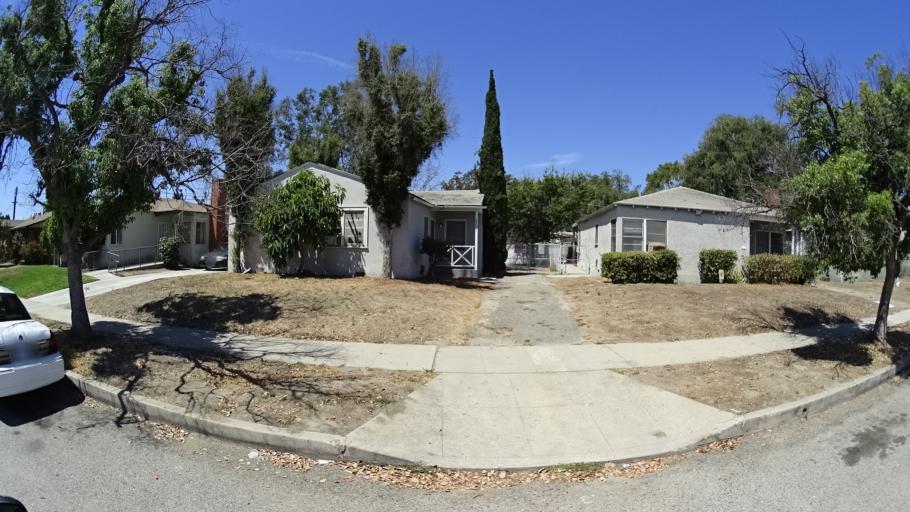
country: US
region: California
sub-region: Los Angeles County
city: North Hollywood
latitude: 34.1861
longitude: -118.3600
